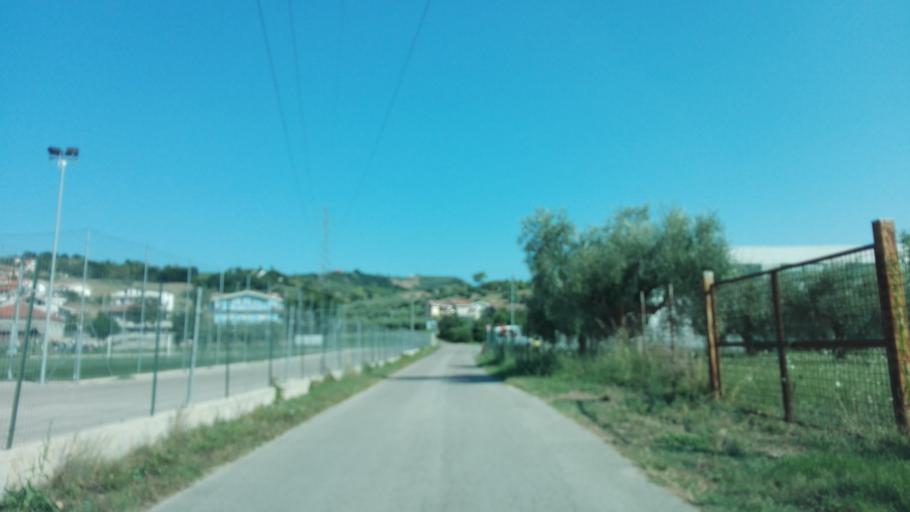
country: IT
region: Abruzzo
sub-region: Provincia di Pescara
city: Cappelle sul Tavo
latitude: 42.4871
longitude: 14.1176
